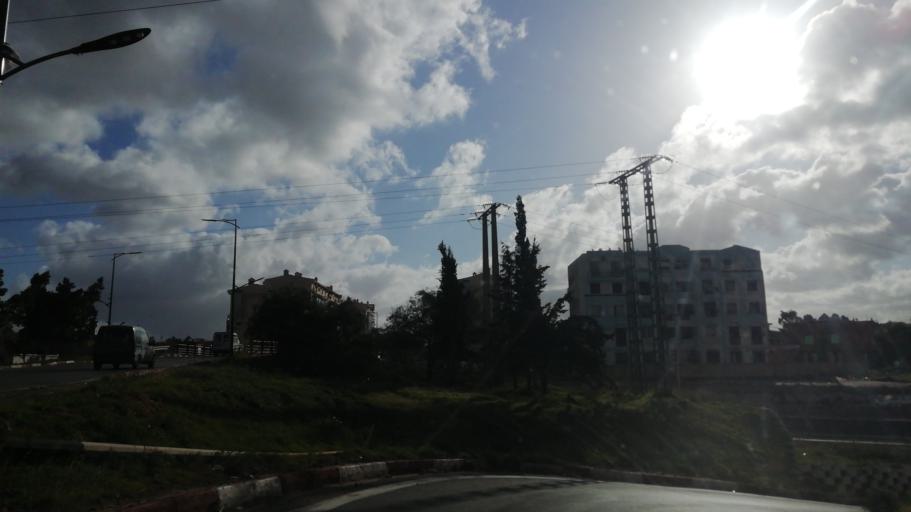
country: DZ
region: Ain Temouchent
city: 'Ain Temouchent
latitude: 35.3028
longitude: -1.1571
